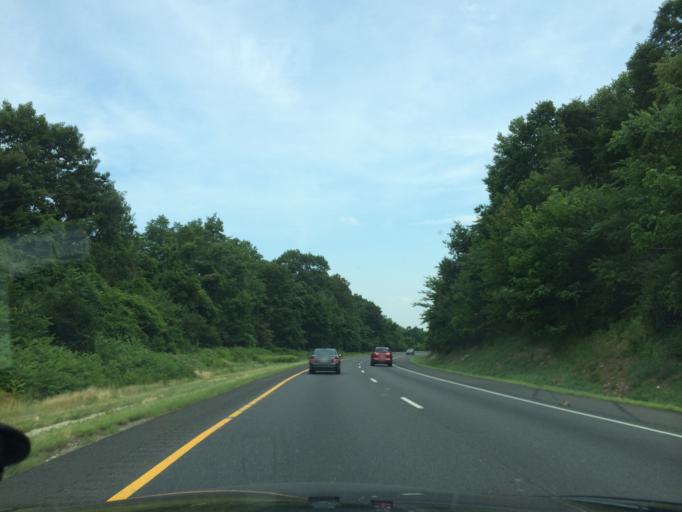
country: US
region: Maryland
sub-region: Frederick County
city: Braddock Heights
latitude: 39.4400
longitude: -77.4925
